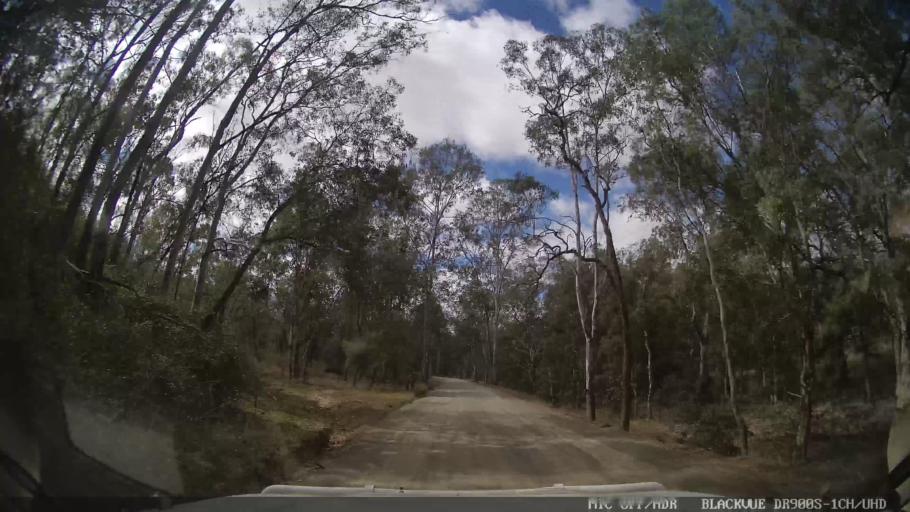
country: AU
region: Queensland
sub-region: Gladstone
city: Toolooa
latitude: -24.5512
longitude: 151.3392
